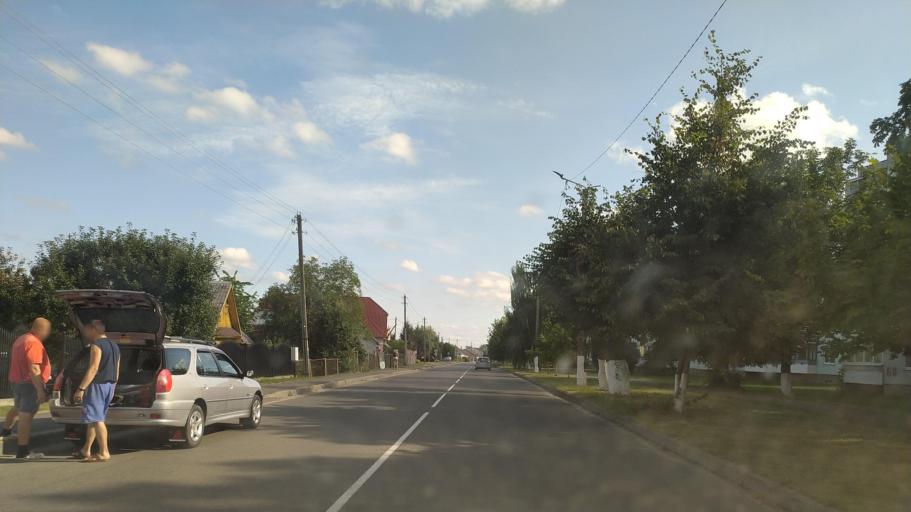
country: BY
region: Brest
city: Byaroza
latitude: 52.5298
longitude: 24.9872
